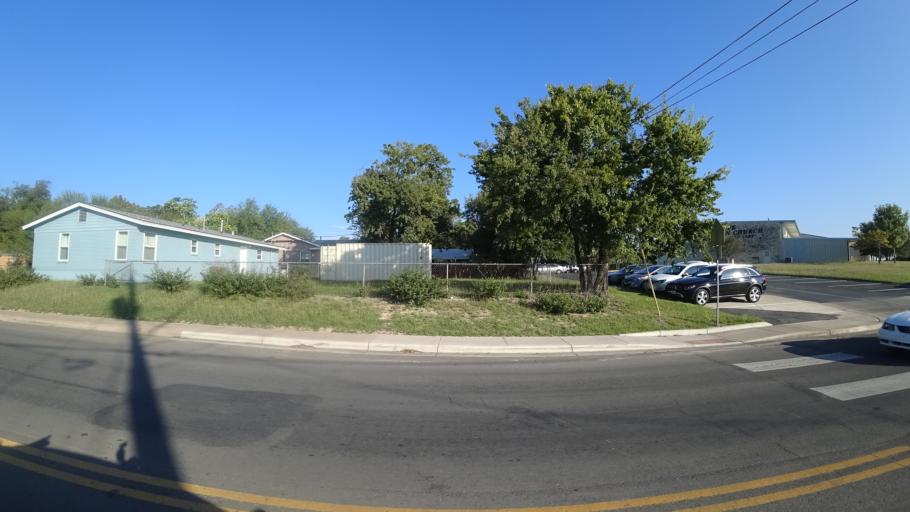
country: US
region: Texas
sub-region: Travis County
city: Austin
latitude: 30.3136
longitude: -97.6820
